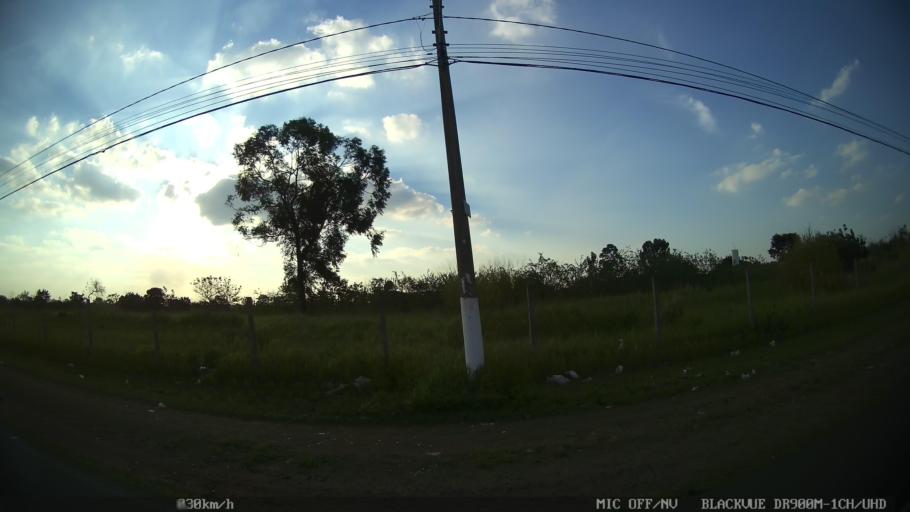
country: BR
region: Sao Paulo
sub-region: Hortolandia
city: Hortolandia
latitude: -22.8620
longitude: -47.1798
